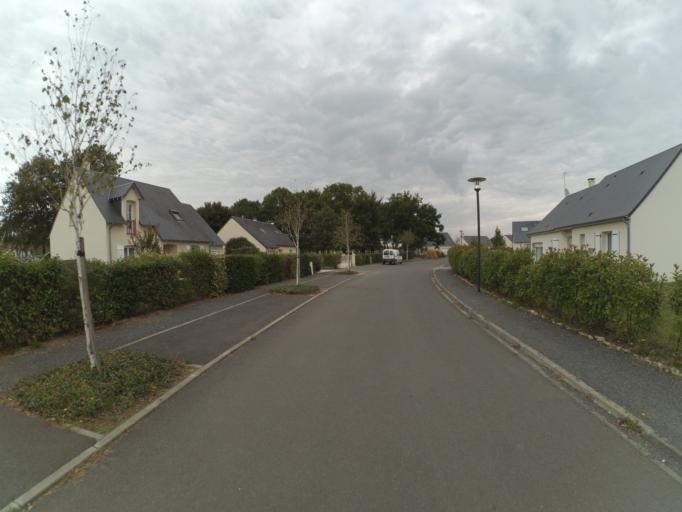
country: FR
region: Centre
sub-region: Departement d'Indre-et-Loire
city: Nazelles-Negron
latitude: 47.4870
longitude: 0.9409
